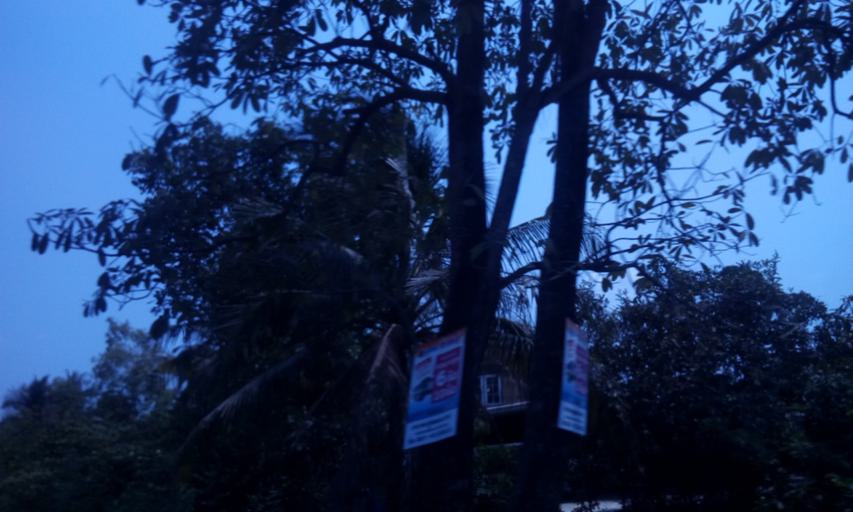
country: TH
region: Chachoengsao
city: Bang Nam Priao
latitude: 13.9087
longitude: 100.9735
